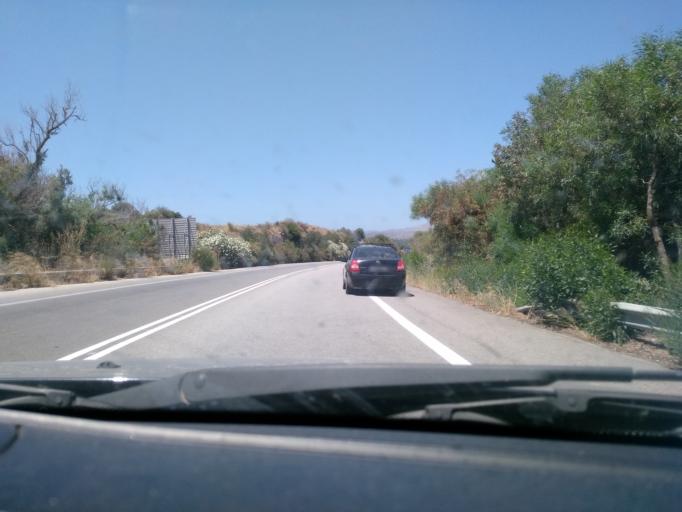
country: GR
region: Crete
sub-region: Nomos Chanias
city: Kalivai
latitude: 35.4320
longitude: 24.1660
